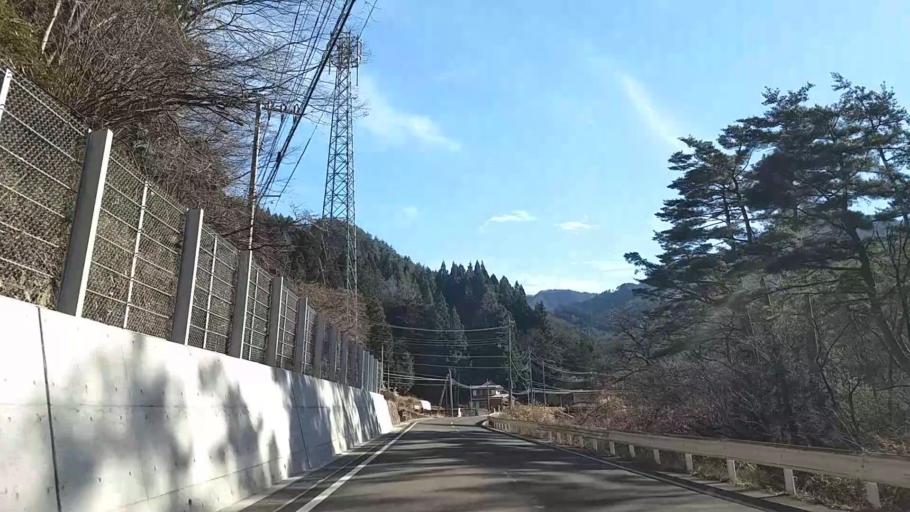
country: JP
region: Yamanashi
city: Otsuki
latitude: 35.5238
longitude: 138.9253
